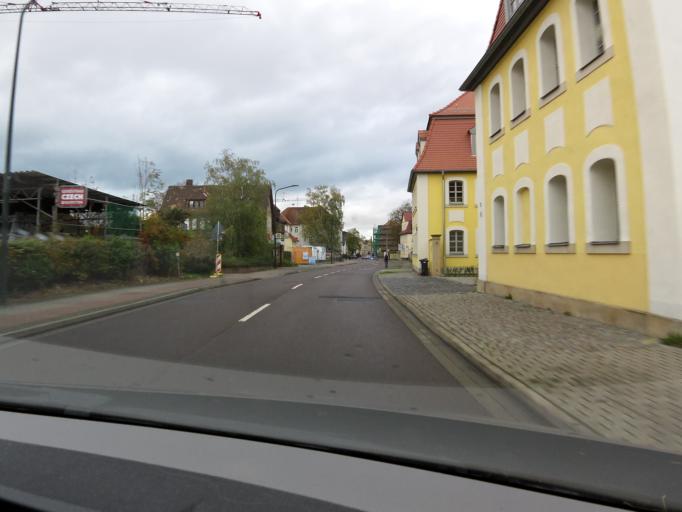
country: DE
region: Saxony
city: Markkleeberg
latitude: 51.2494
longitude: 12.3801
